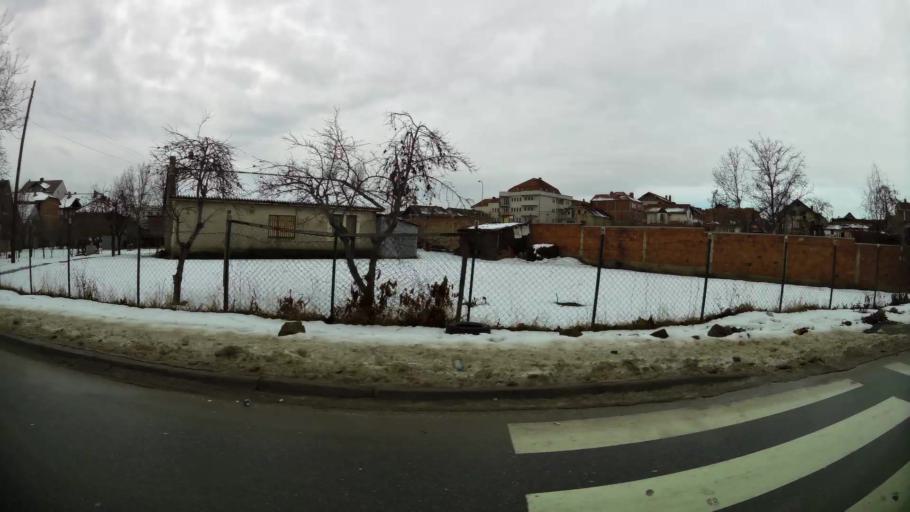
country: XK
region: Pristina
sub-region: Komuna e Prishtines
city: Pristina
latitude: 42.6777
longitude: 21.1729
